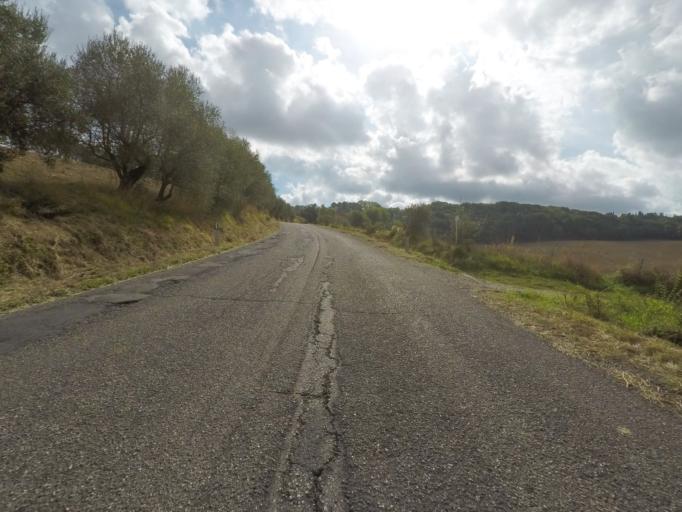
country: IT
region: Tuscany
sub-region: Provincia di Siena
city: Torrita di Siena
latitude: 43.1572
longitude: 11.7751
